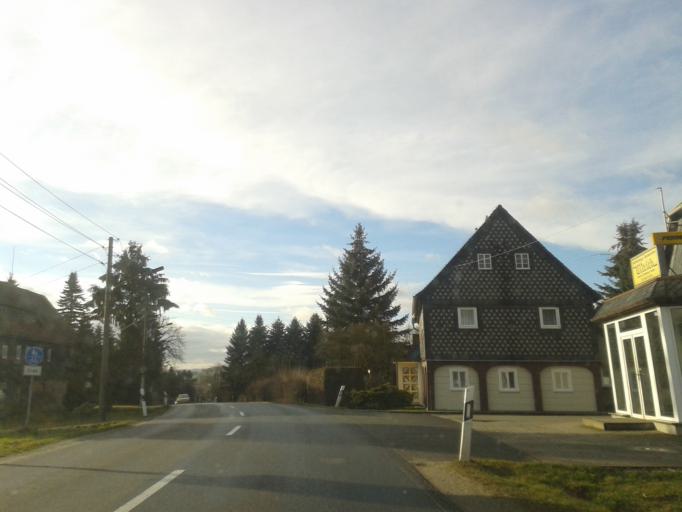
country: DE
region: Saxony
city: Herrnhut
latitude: 50.9921
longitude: 14.7119
